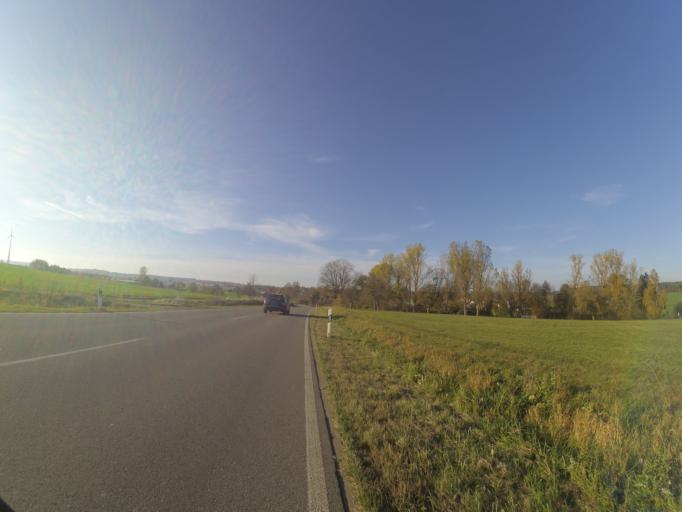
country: DE
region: Baden-Wuerttemberg
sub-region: Tuebingen Region
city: Berghulen
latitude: 48.4547
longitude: 9.7862
